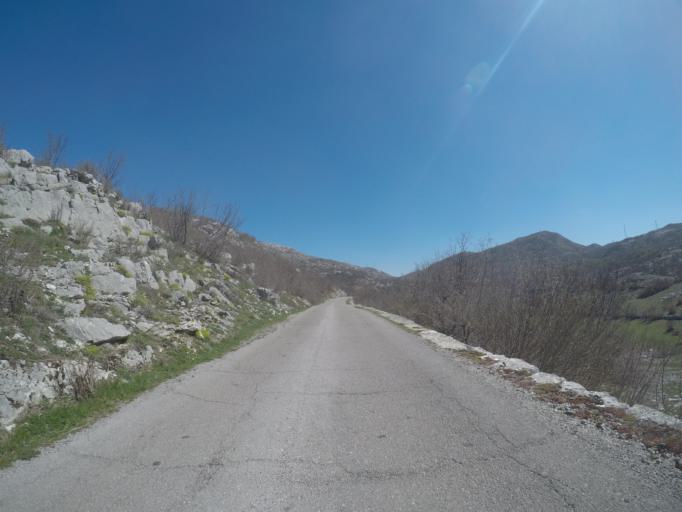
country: ME
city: Dobrota
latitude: 42.4925
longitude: 18.8687
